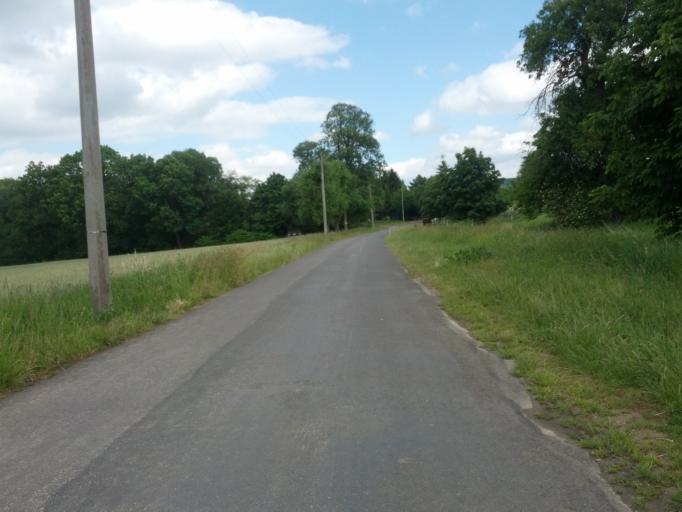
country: DE
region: Thuringia
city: Eisenach
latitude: 50.9774
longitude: 10.3671
